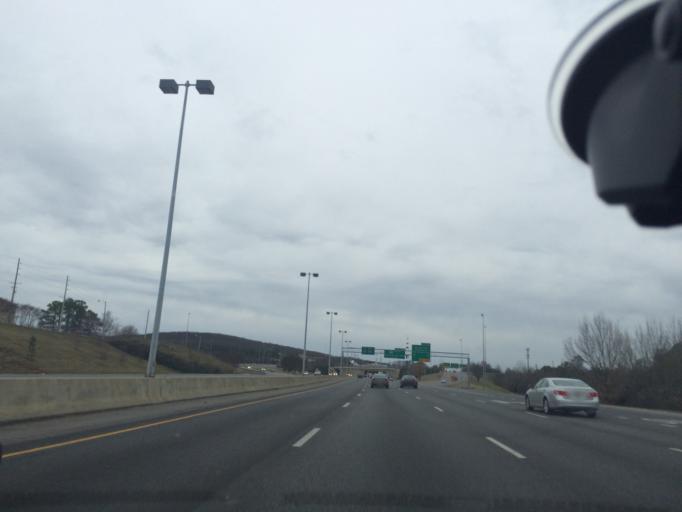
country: US
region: Alabama
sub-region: Madison County
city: Redstone Arsenal
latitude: 34.7174
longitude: -86.6375
